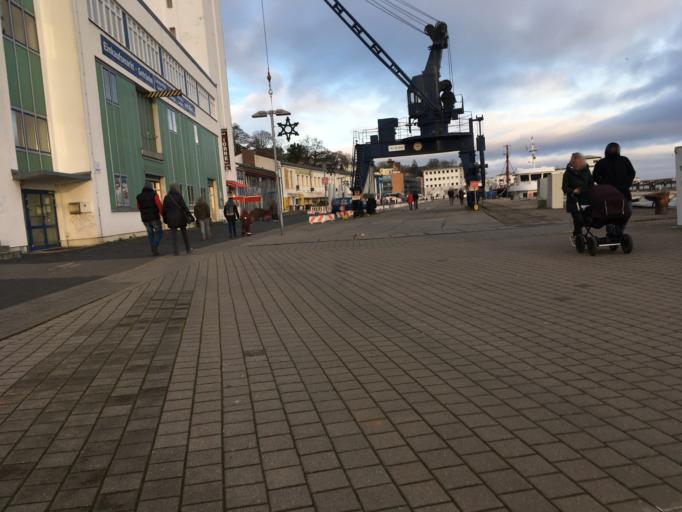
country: DE
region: Mecklenburg-Vorpommern
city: Sassnitz
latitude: 54.5131
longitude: 13.6428
